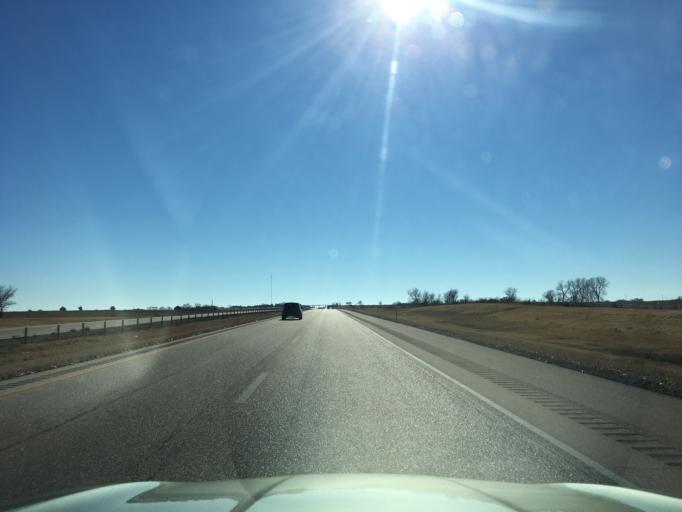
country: US
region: Oklahoma
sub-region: Kay County
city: Blackwell
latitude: 36.8834
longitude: -97.3519
